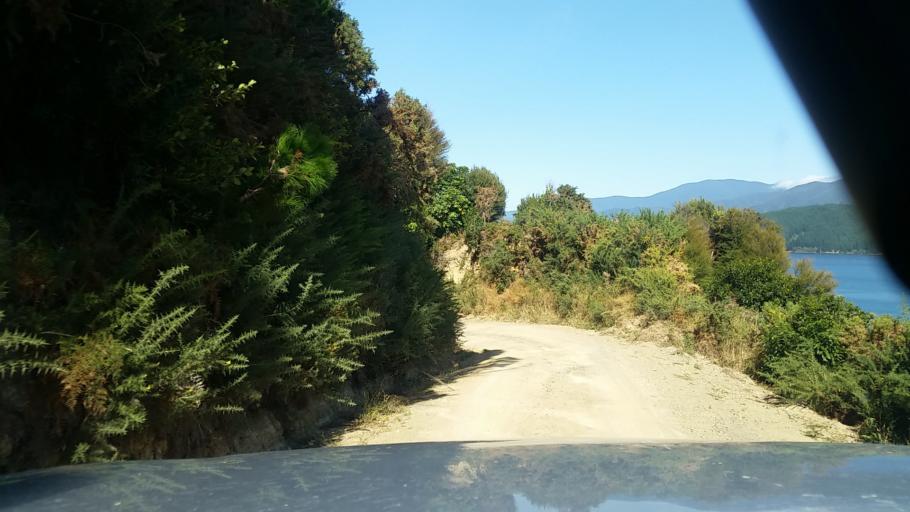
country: NZ
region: Marlborough
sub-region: Marlborough District
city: Picton
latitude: -41.3007
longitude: 174.1785
